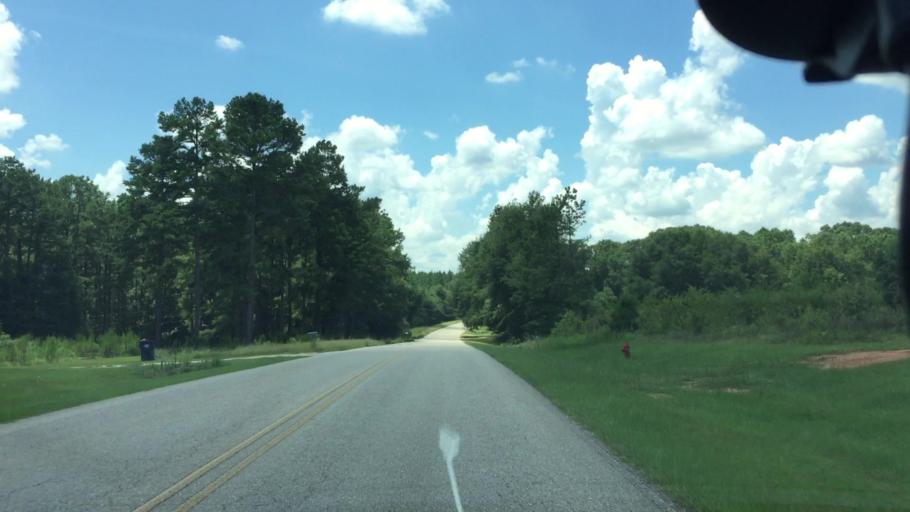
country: US
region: Alabama
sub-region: Pike County
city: Troy
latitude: 31.7472
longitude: -85.9701
